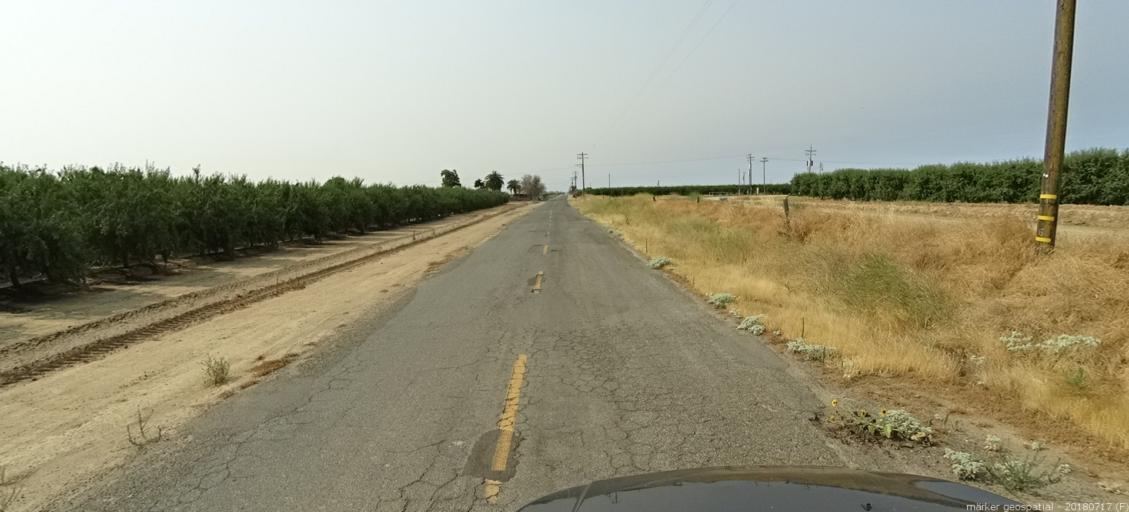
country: US
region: California
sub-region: Madera County
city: Fairmead
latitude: 37.0995
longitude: -120.1109
